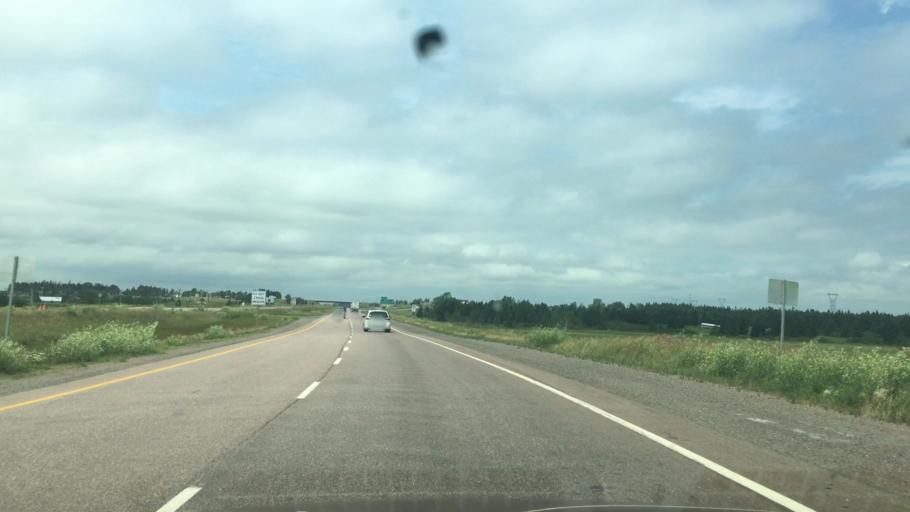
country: CA
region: Nova Scotia
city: Amherst
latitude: 45.8472
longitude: -64.2419
